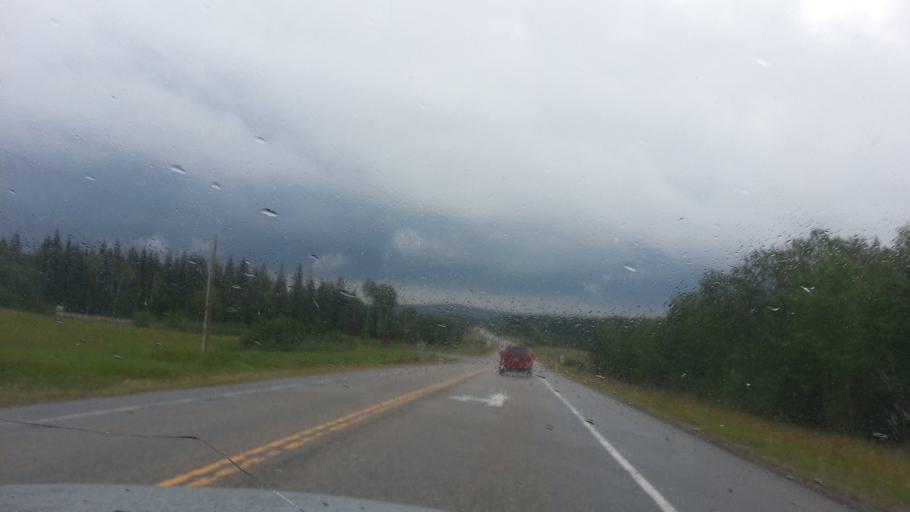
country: CA
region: Alberta
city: Cochrane
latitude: 50.9214
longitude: -114.5866
